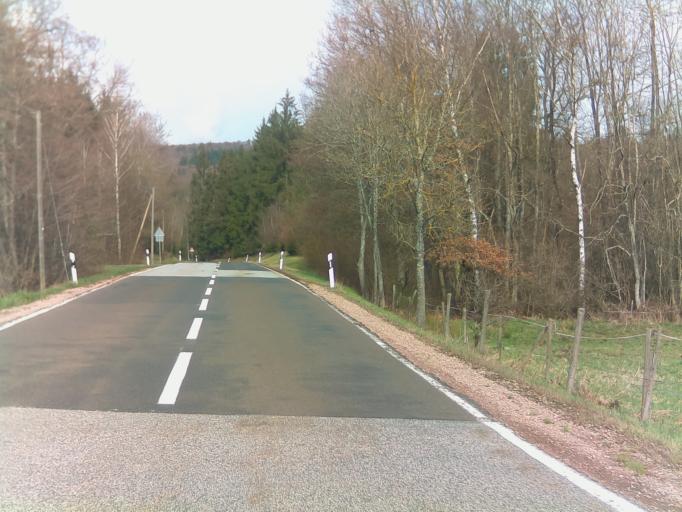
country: DE
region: Rheinland-Pfalz
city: Munchwald
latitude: 49.9190
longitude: 7.6648
